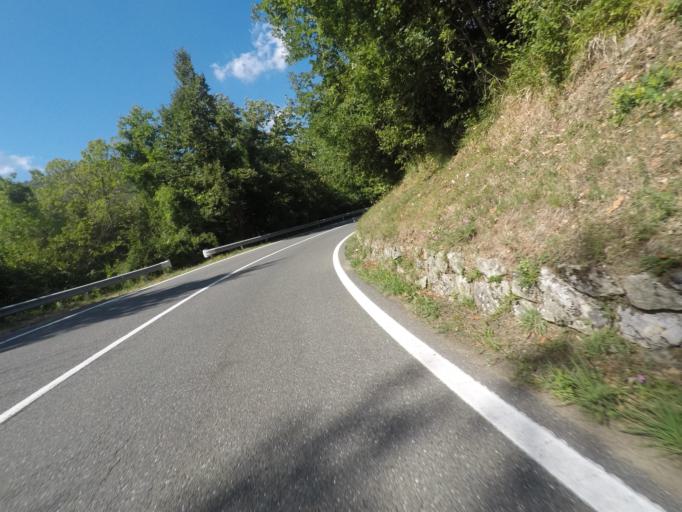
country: IT
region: Tuscany
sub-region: Provincia di Massa-Carrara
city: Fivizzano
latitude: 44.2452
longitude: 10.1644
